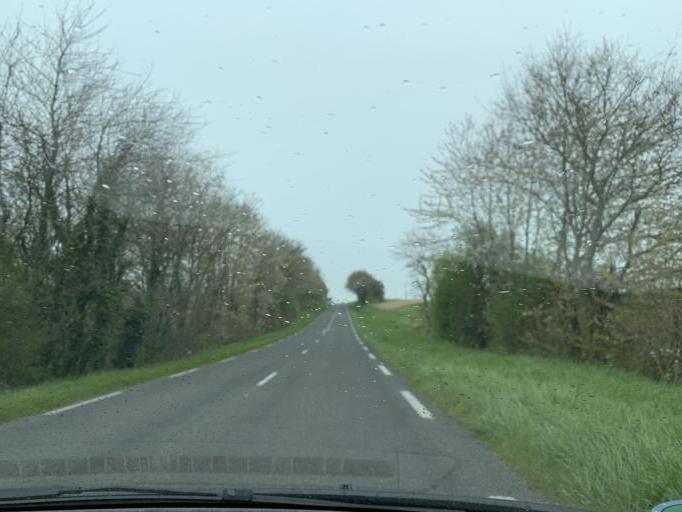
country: FR
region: Haute-Normandie
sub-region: Departement de la Seine-Maritime
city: Cany-Barville
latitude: 49.8068
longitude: 0.6675
